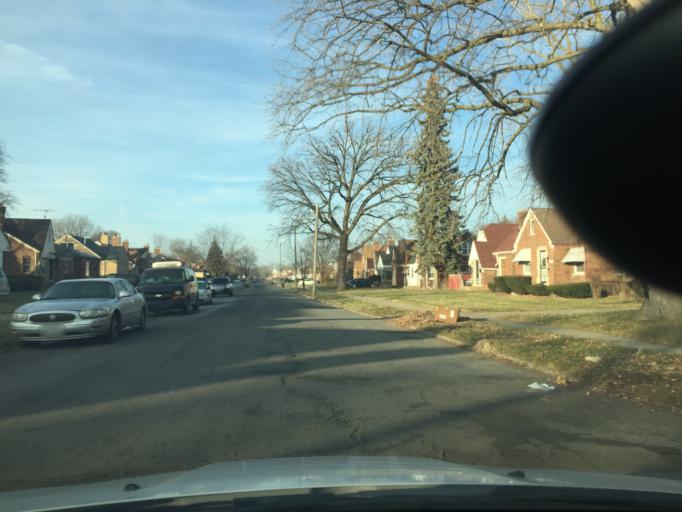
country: US
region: Michigan
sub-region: Macomb County
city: Eastpointe
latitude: 42.4446
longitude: -82.9636
